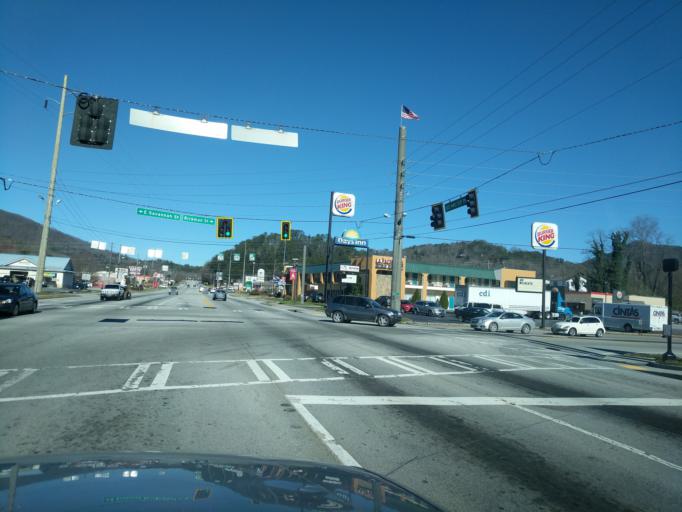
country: US
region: Georgia
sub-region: Rabun County
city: Clayton
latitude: 34.8775
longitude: -83.3972
